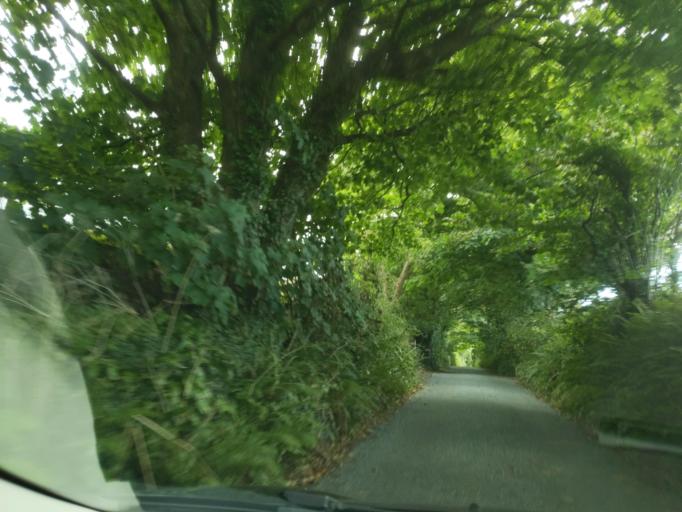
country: GB
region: England
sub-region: Plymouth
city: Plymstock
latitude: 50.3477
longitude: -4.1064
